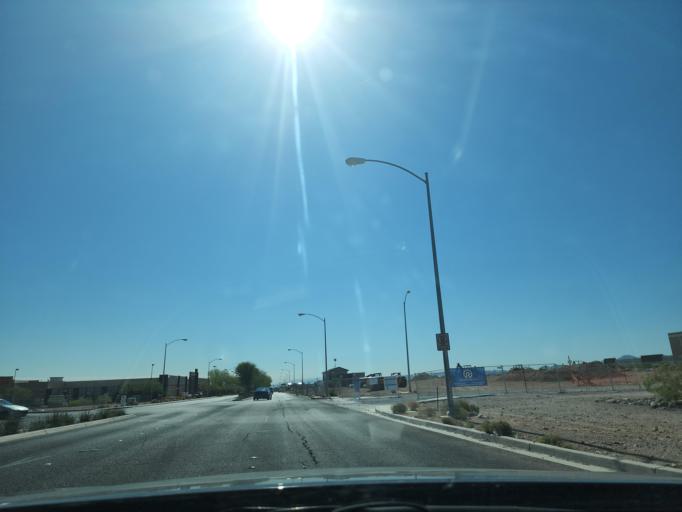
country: US
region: Nevada
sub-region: Clark County
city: Enterprise
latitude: 36.0612
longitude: -115.2478
